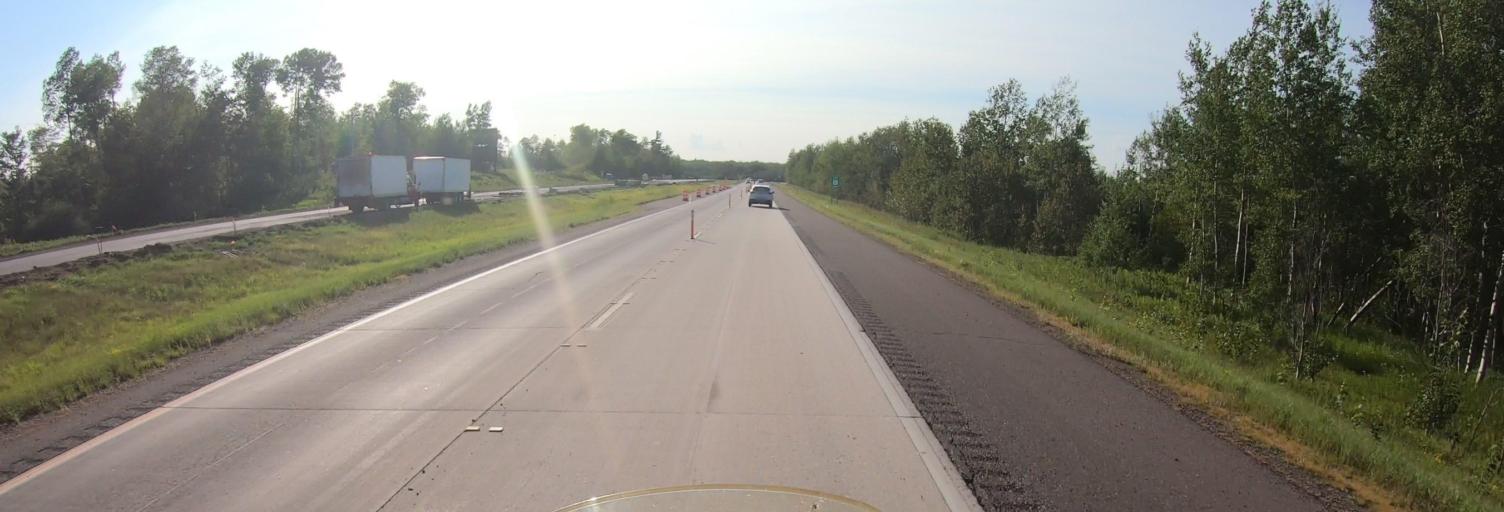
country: US
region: Minnesota
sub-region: Saint Louis County
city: Hermantown
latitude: 46.9219
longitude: -92.4051
